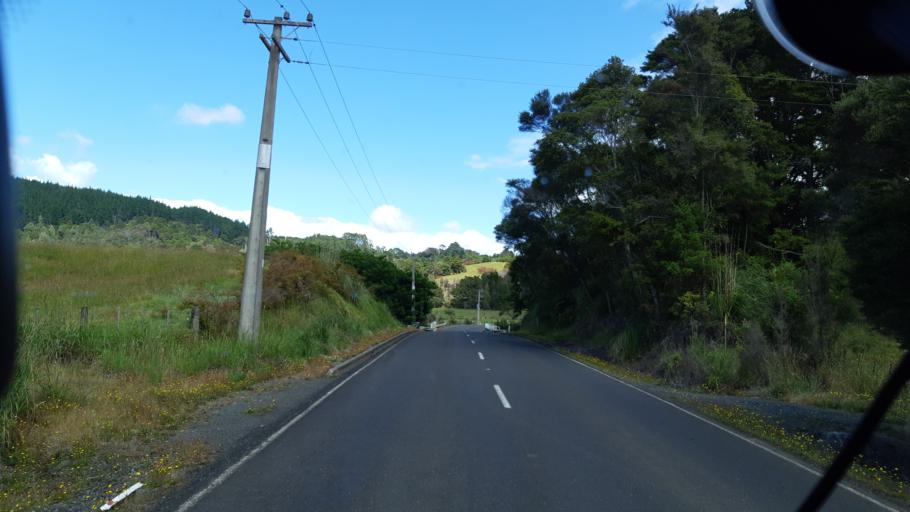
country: NZ
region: Northland
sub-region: Far North District
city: Taipa
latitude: -35.2726
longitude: 173.5116
